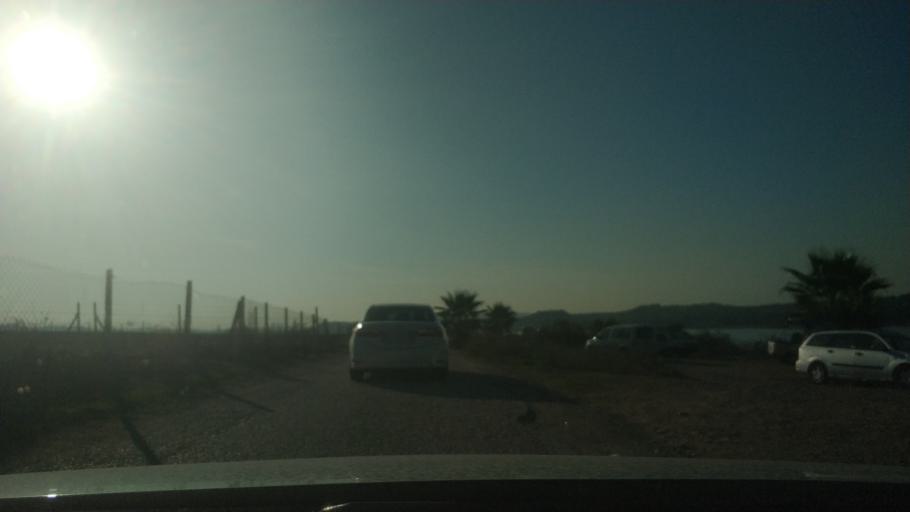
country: TR
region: Adana
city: Adana
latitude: 37.0964
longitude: 35.3030
